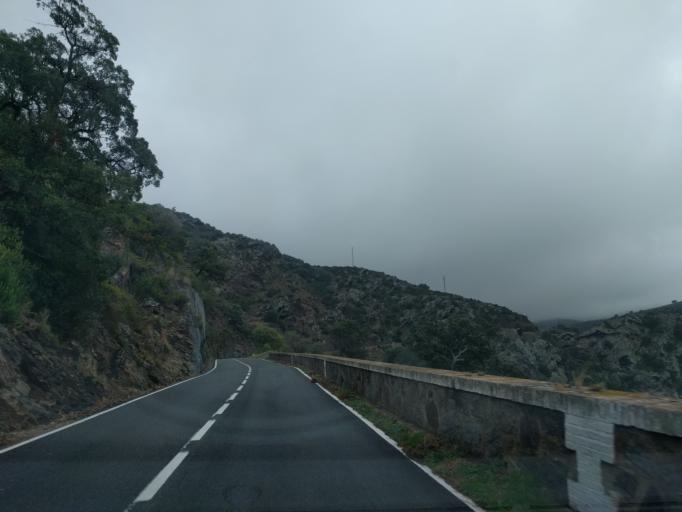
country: ES
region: Catalonia
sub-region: Provincia de Girona
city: Cadaques
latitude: 42.3043
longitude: 3.2271
